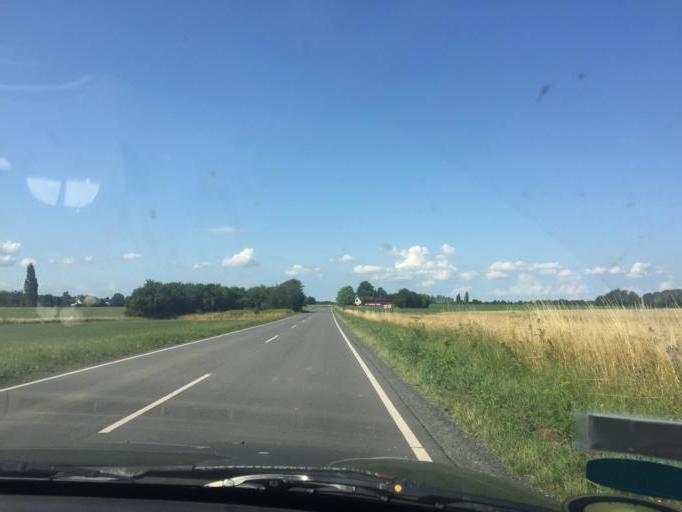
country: DK
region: Zealand
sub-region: Lolland Kommune
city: Maribo
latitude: 54.7966
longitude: 11.5481
